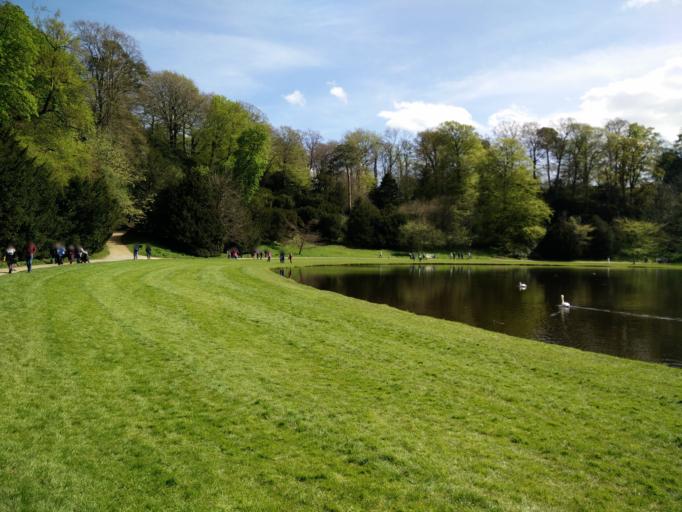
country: GB
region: England
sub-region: North Yorkshire
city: Ripon
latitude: 54.1126
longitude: -1.5709
